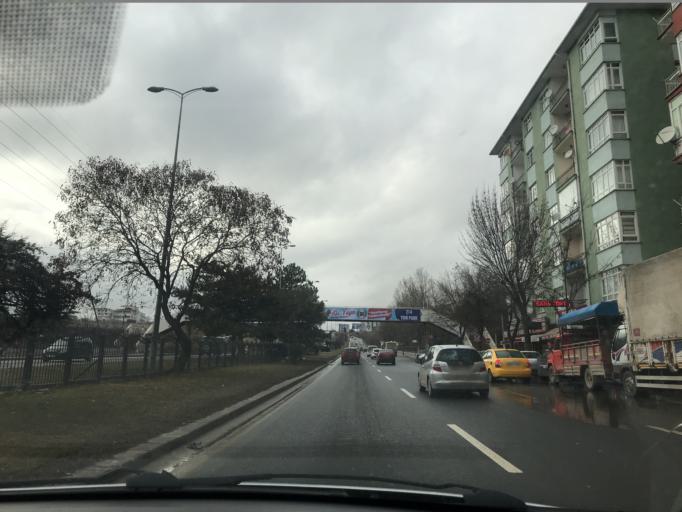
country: TR
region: Ankara
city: Batikent
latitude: 39.9586
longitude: 32.7879
